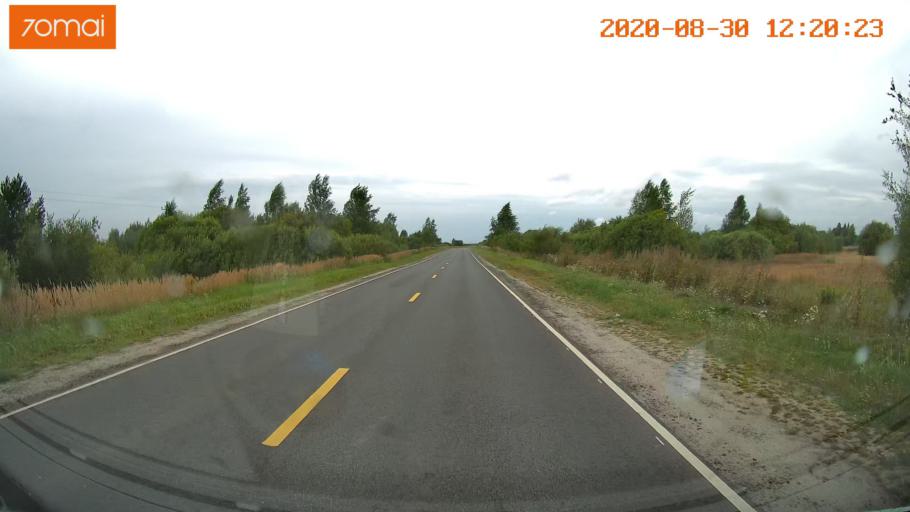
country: RU
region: Ivanovo
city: Yur'yevets
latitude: 57.3228
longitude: 42.9020
